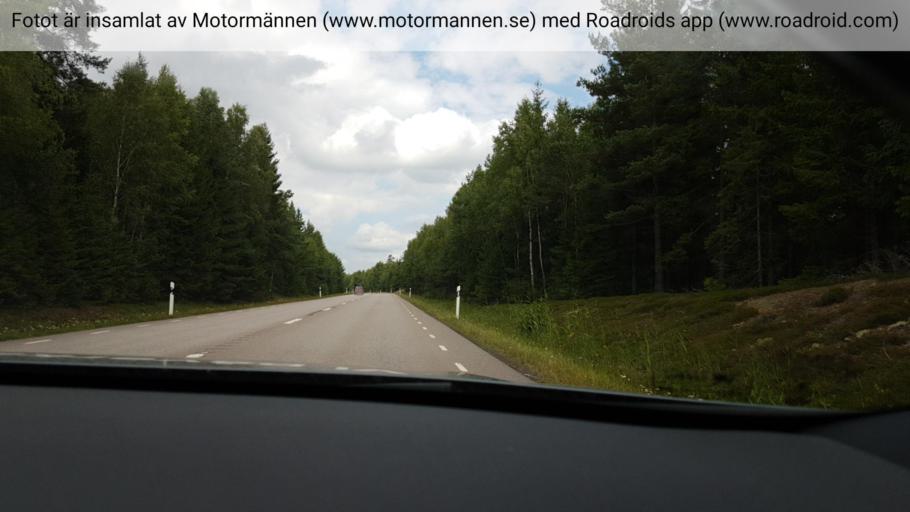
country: SE
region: Vaestra Goetaland
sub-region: Skara Kommun
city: Skara
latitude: 58.3021
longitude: 13.4682
